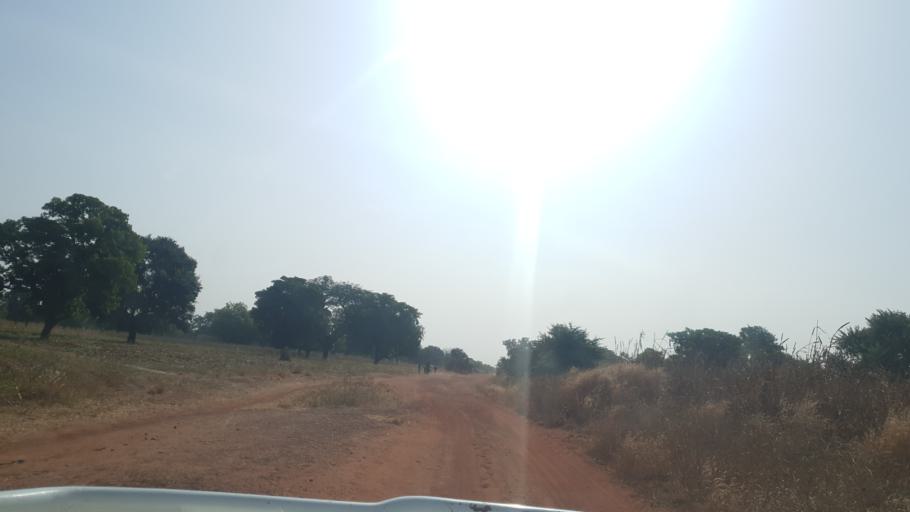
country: ML
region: Koulikoro
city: Dioila
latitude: 12.7051
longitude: -6.7691
